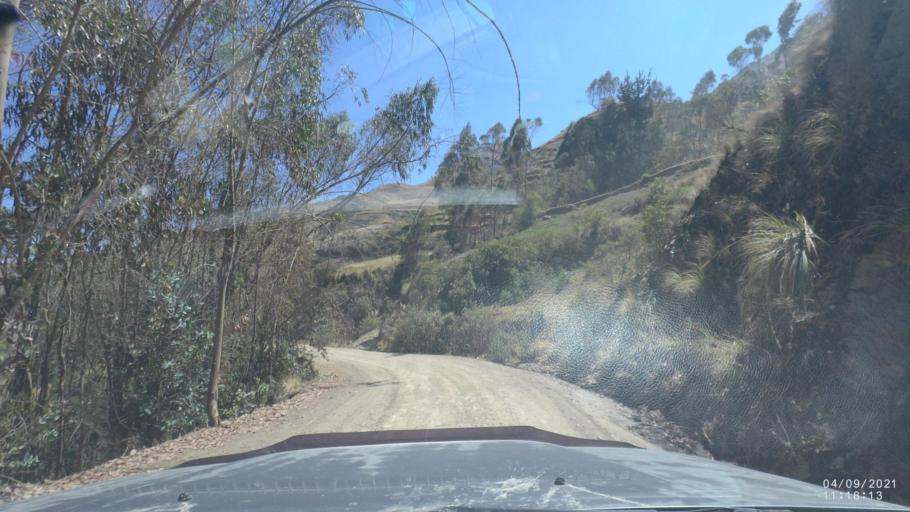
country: BO
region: Cochabamba
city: Sipe Sipe
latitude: -17.2675
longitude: -66.4923
